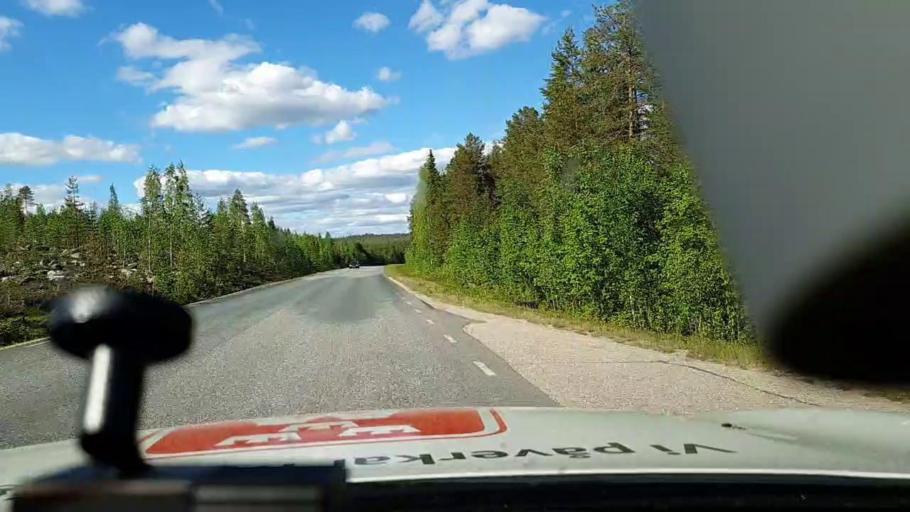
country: FI
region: Lapland
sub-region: Torniolaakso
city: Ylitornio
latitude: 66.3176
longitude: 23.6199
